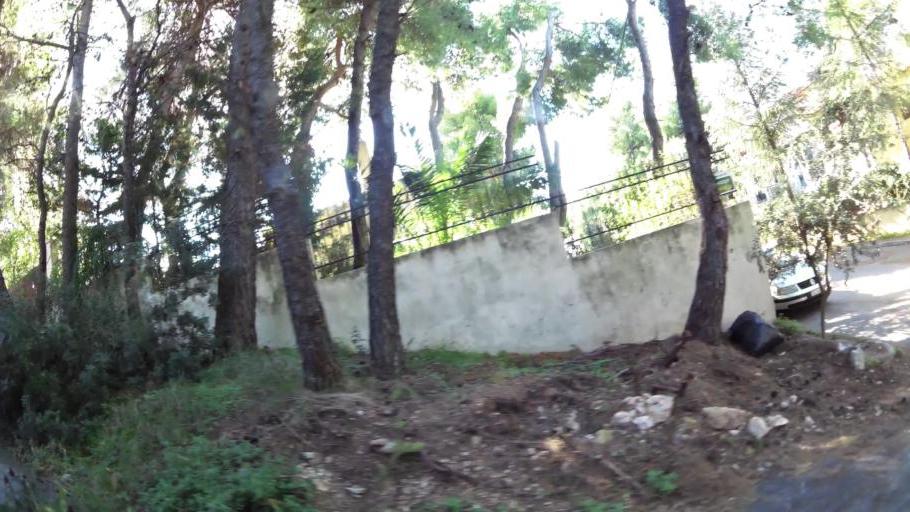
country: GR
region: Attica
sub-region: Nomarchia Anatolikis Attikis
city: Drosia
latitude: 38.1259
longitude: 23.8626
